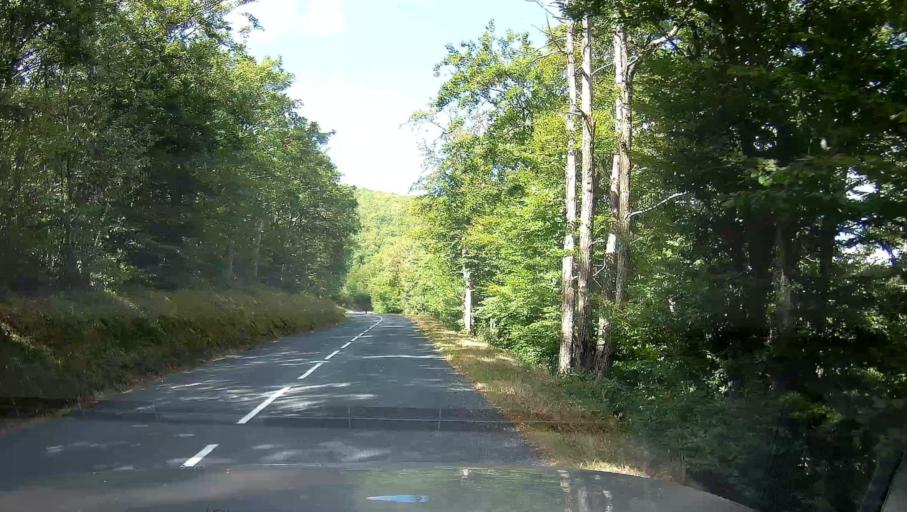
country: FR
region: Rhone-Alpes
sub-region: Departement du Rhone
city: Cogny
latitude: 45.9879
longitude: 4.5718
